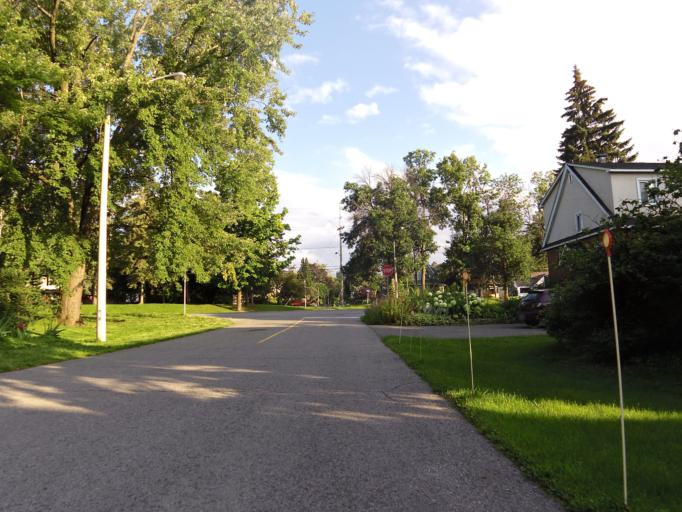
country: CA
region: Ontario
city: Ottawa
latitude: 45.3866
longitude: -75.7643
